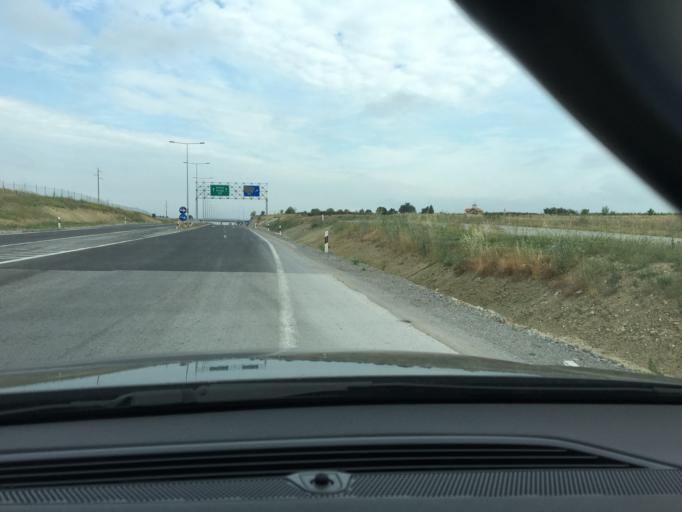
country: MK
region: Stip
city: Shtip
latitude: 41.7777
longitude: 22.1321
